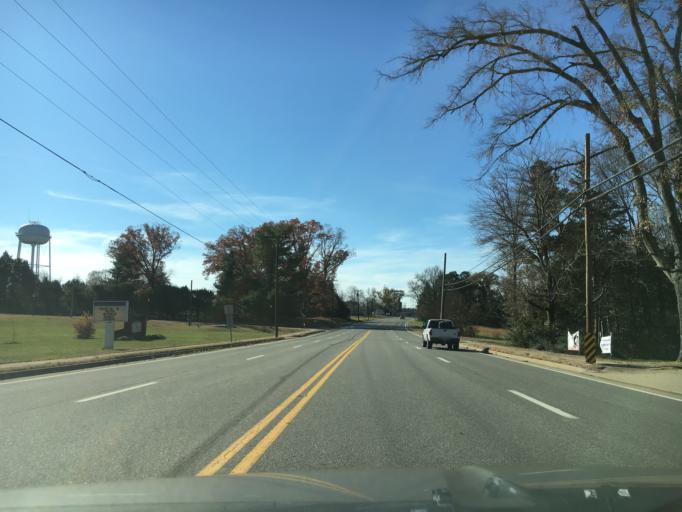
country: US
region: Virginia
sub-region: Cumberland County
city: Cumberland
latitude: 37.4931
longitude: -78.2487
